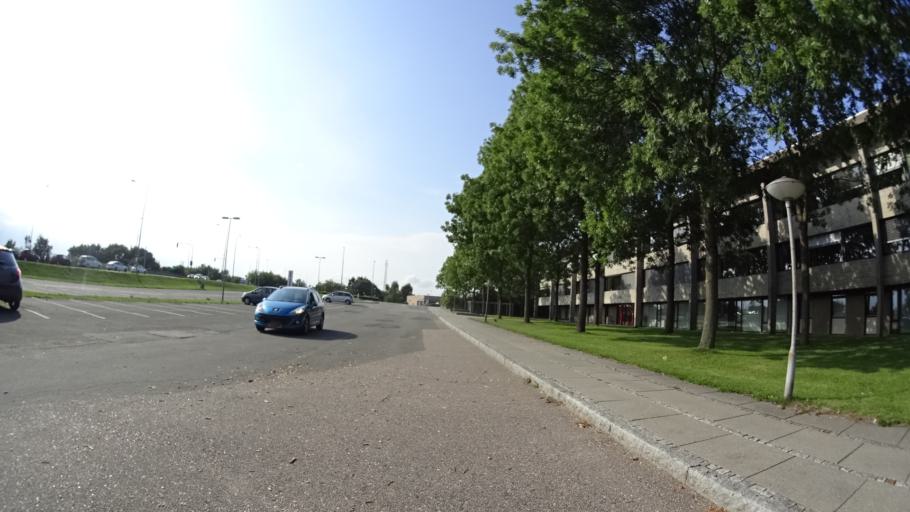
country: DK
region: Central Jutland
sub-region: Arhus Kommune
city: Stavtrup
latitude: 56.1532
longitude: 10.1190
